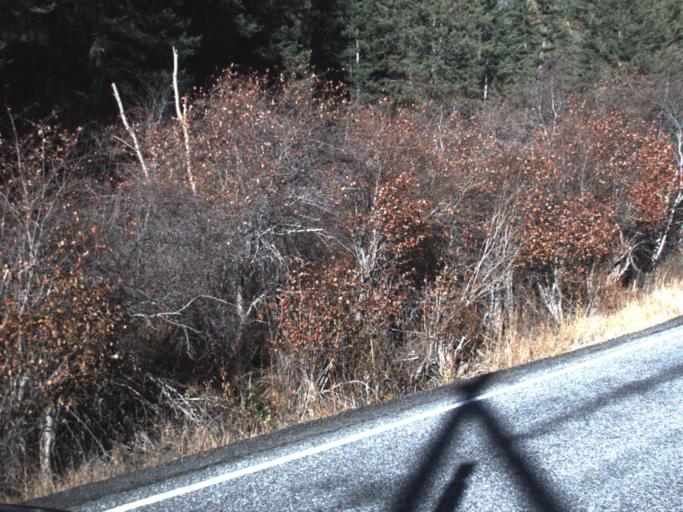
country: US
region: Washington
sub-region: Ferry County
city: Republic
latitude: 48.5459
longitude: -118.7490
